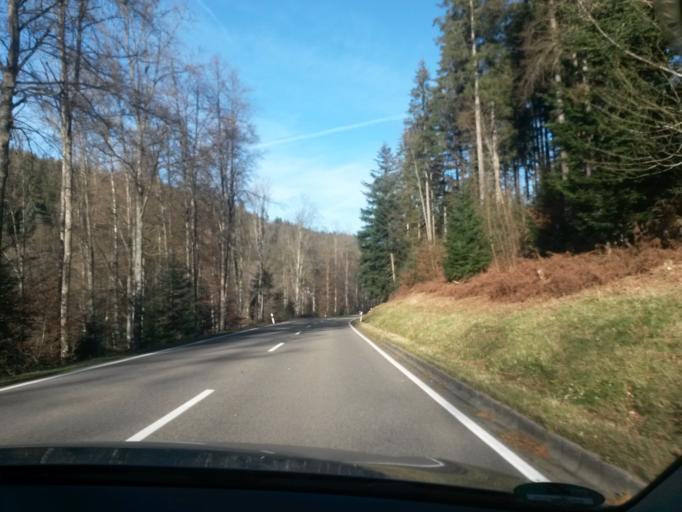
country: DE
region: Baden-Wuerttemberg
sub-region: Karlsruhe Region
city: Bad Wildbad
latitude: 48.7185
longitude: 8.5619
